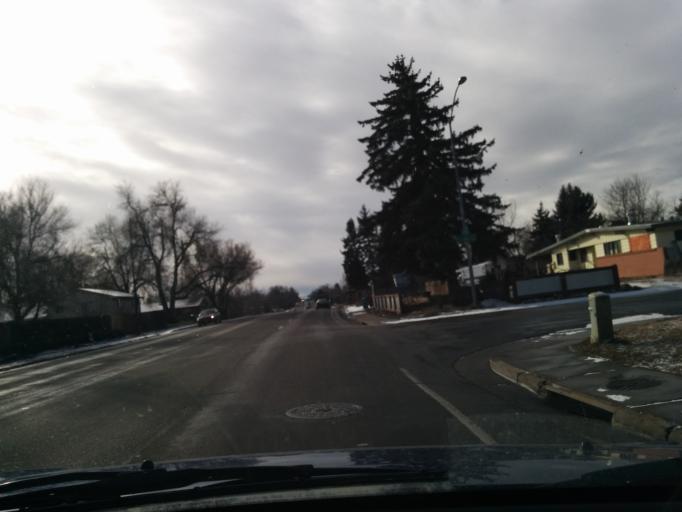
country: US
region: Colorado
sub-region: Larimer County
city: Fort Collins
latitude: 40.5693
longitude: -105.1151
